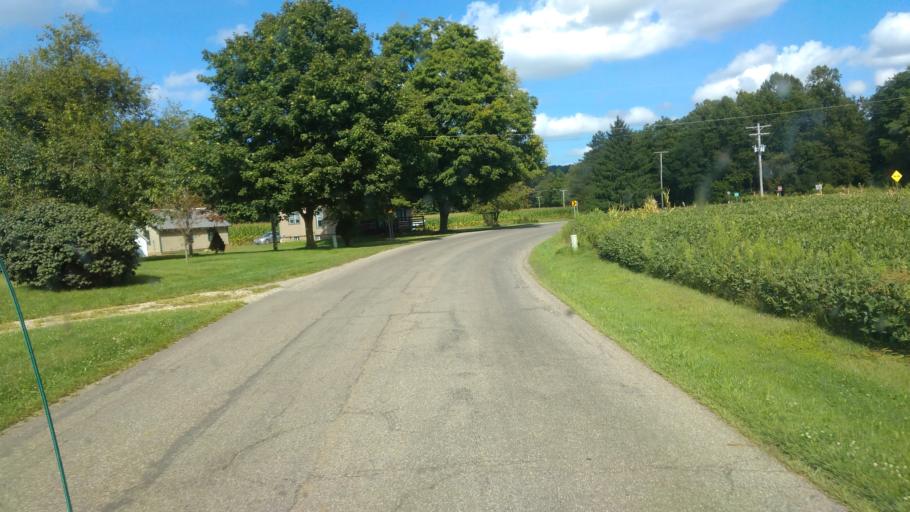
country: US
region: Ohio
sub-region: Holmes County
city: Millersburg
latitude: 40.6450
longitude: -81.8908
